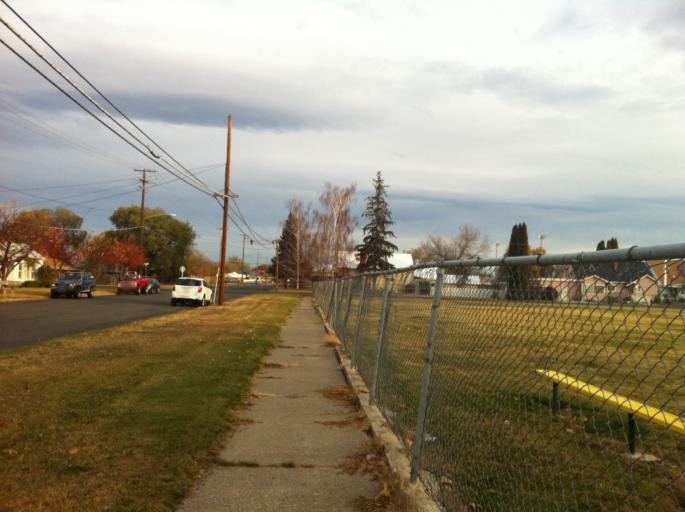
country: US
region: Oregon
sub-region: Baker County
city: Baker City
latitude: 44.7846
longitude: -117.8397
